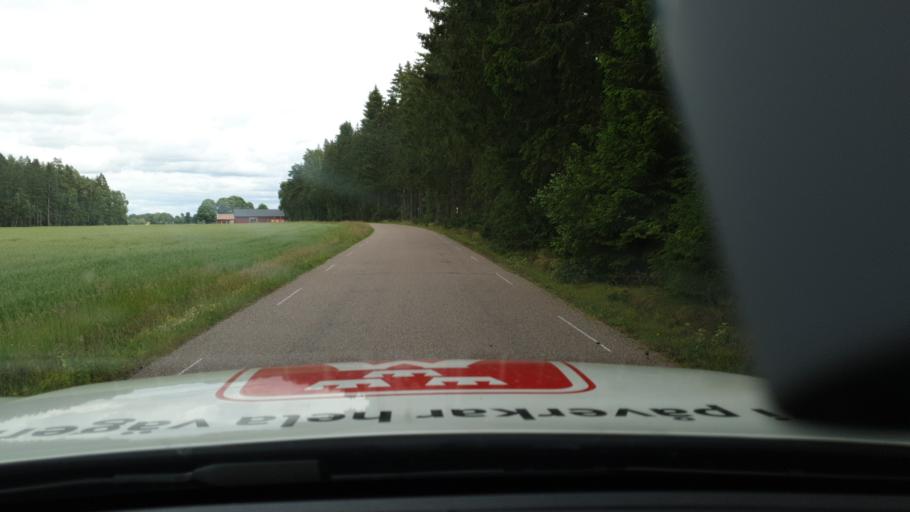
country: SE
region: Vaestra Goetaland
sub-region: Skara Kommun
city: Skara
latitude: 58.3971
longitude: 13.3539
